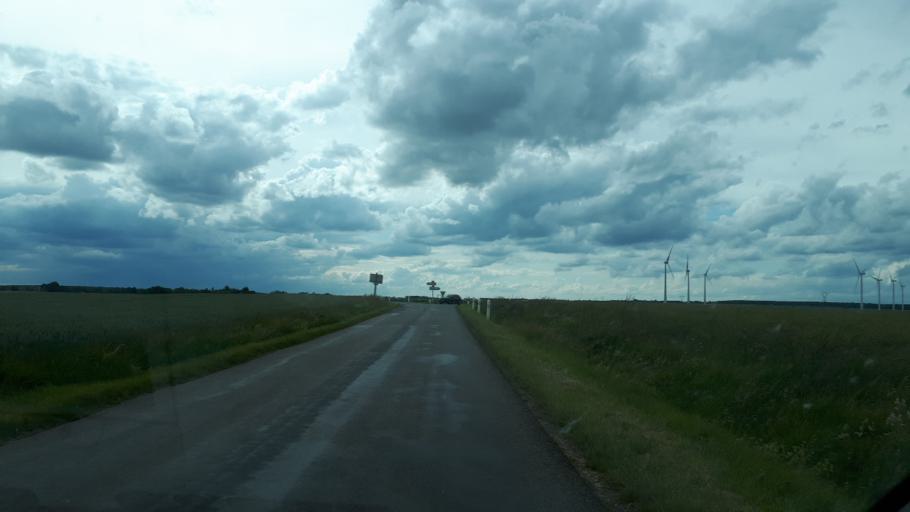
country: FR
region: Centre
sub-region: Departement du Cher
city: Massay
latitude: 47.1018
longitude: 1.9553
